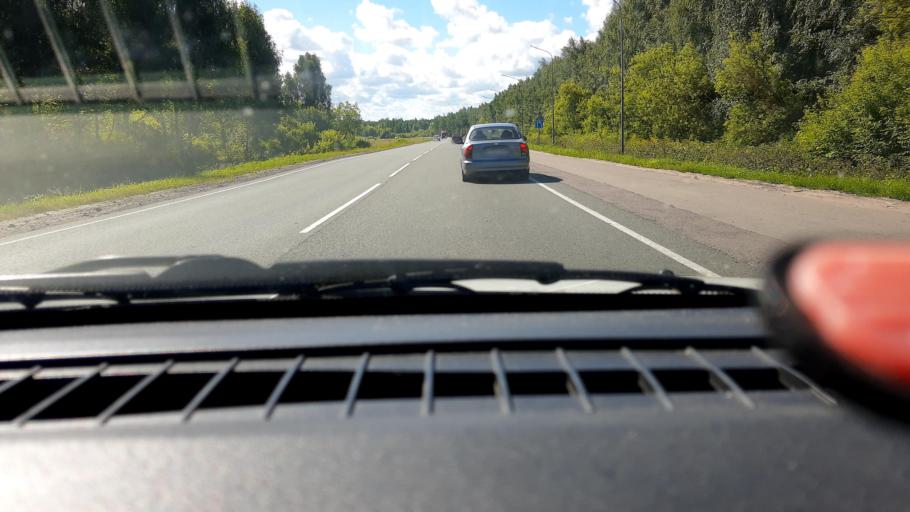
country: RU
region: Nizjnij Novgorod
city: Arzamas
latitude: 55.3227
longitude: 43.8880
